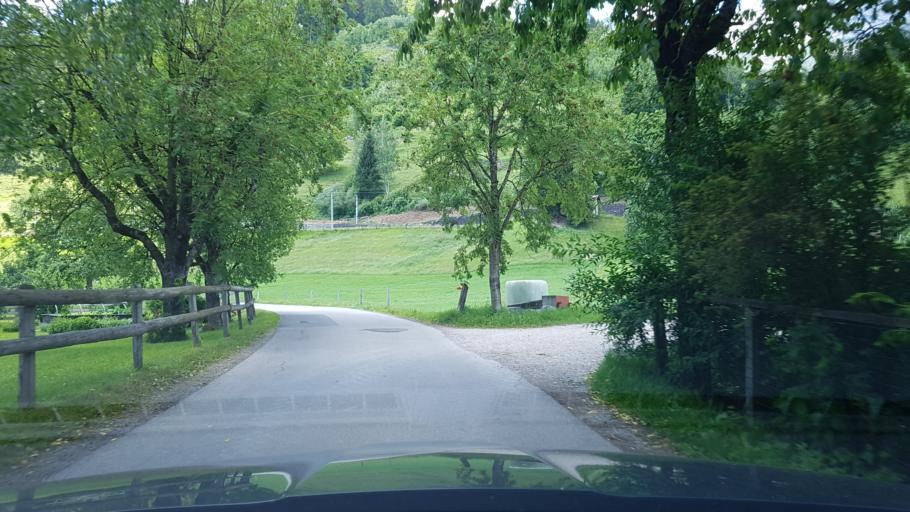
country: AT
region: Salzburg
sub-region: Politischer Bezirk Zell am See
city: Leogang
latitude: 47.4449
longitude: 12.7836
